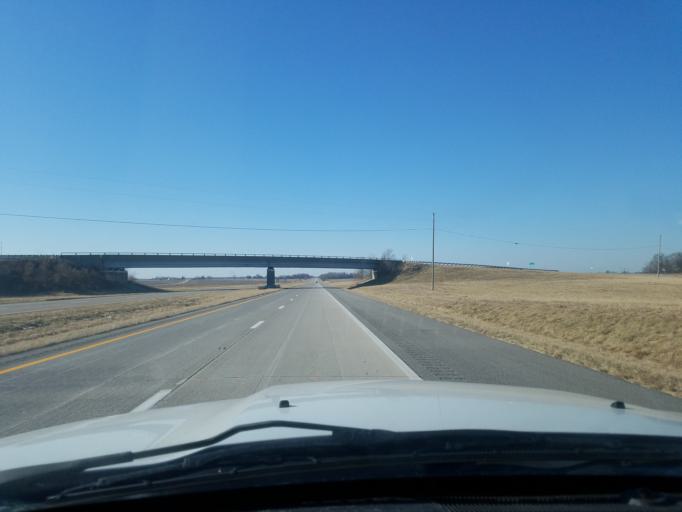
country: US
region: Kentucky
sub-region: Henderson County
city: Henderson
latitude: 37.7858
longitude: -87.4701
